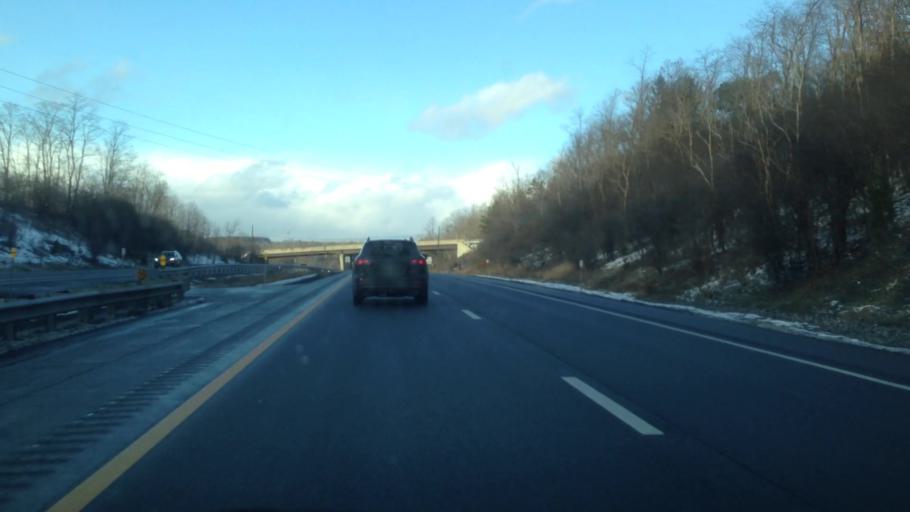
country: US
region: New York
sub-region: Schenectady County
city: Rotterdam
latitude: 42.8037
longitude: -74.0180
